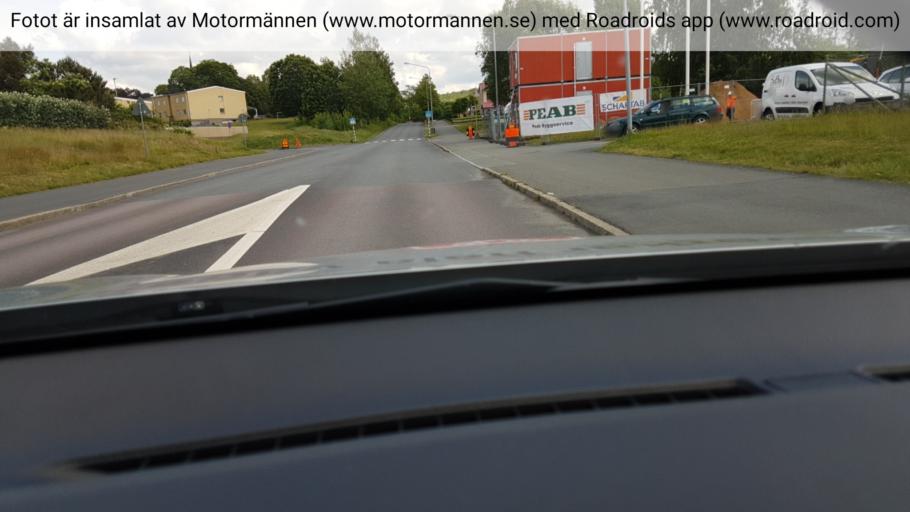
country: SE
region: Joenkoeping
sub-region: Jonkopings Kommun
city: Jonkoping
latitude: 57.7535
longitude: 14.1711
